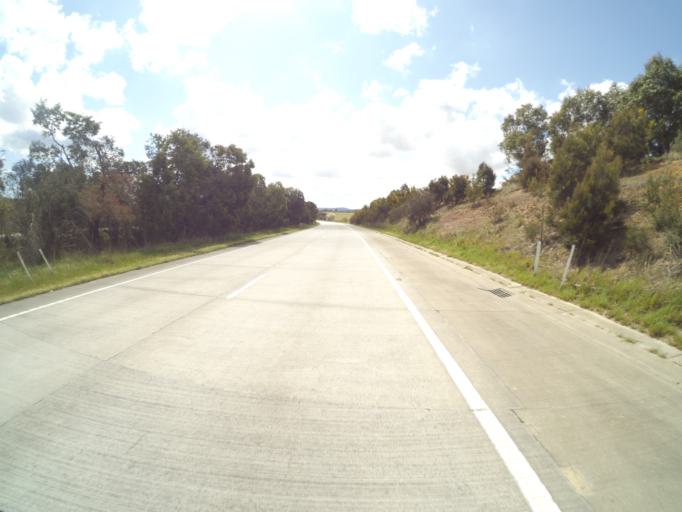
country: AU
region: New South Wales
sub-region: Wingecarribee
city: Moss Vale
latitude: -34.5109
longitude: 150.3082
